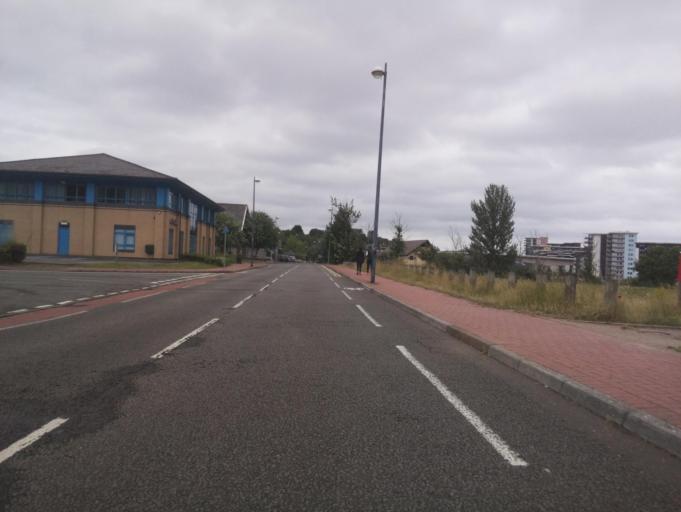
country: GB
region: Wales
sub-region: Vale of Glamorgan
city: Penarth
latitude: 51.4454
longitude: -3.1835
